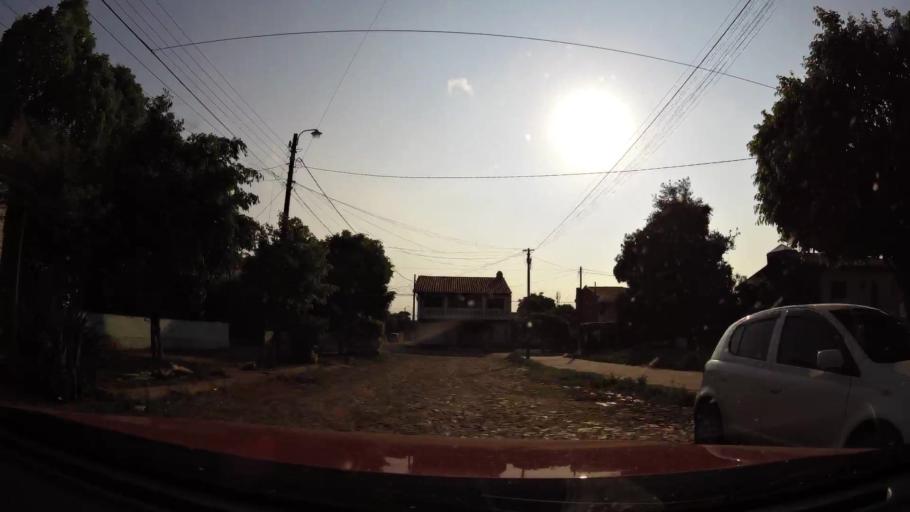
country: PY
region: Central
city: Lambare
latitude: -25.3455
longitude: -57.5979
